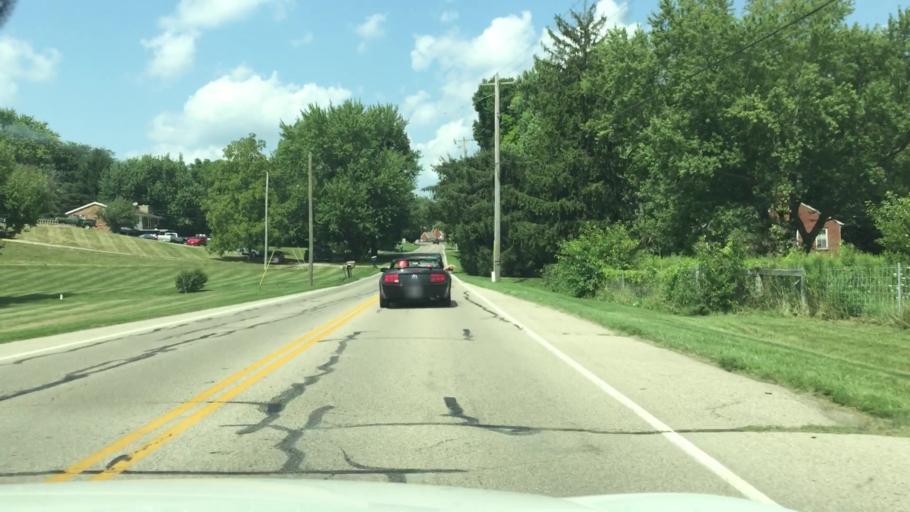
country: US
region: Ohio
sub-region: Clark County
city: Northridge
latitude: 39.9358
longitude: -83.7321
